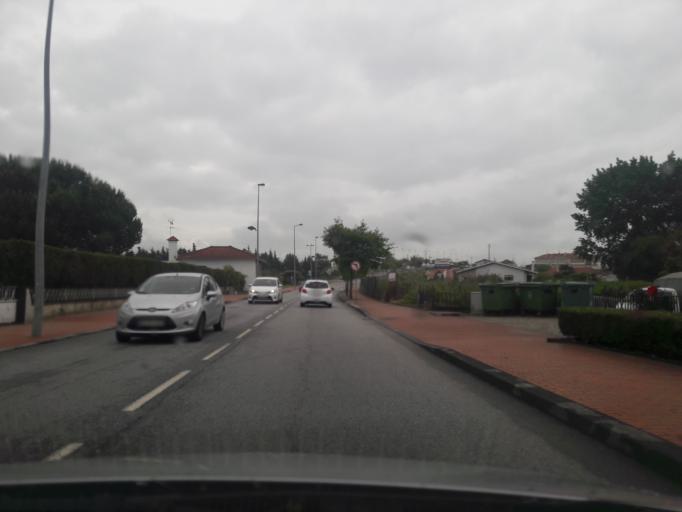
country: PT
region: Porto
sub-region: Vila do Conde
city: Arvore
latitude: 41.3361
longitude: -8.7241
